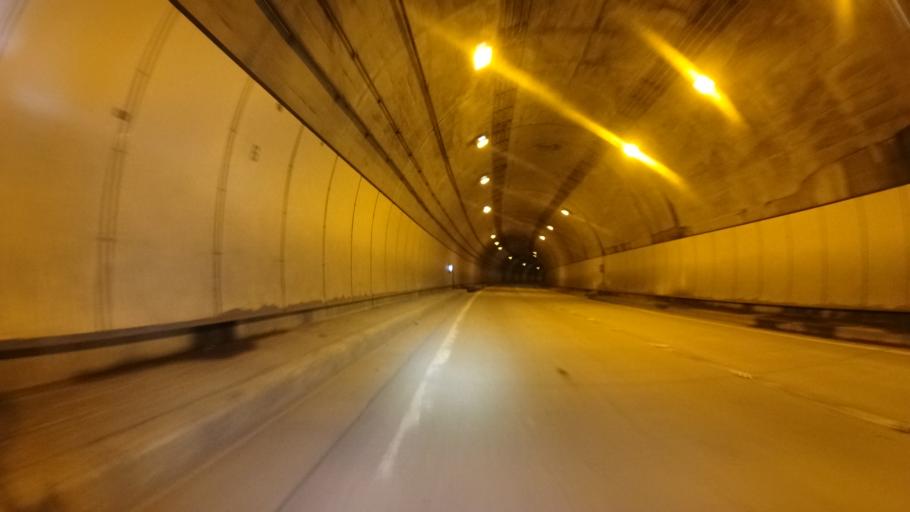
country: JP
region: Yamanashi
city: Uenohara
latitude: 35.6958
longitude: 139.1037
